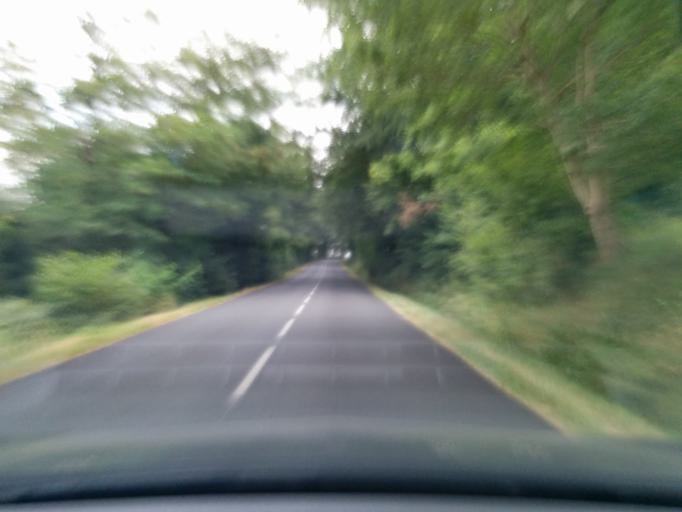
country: FR
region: Midi-Pyrenees
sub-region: Departement de la Haute-Garonne
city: Venerque
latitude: 43.4724
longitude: 1.4514
